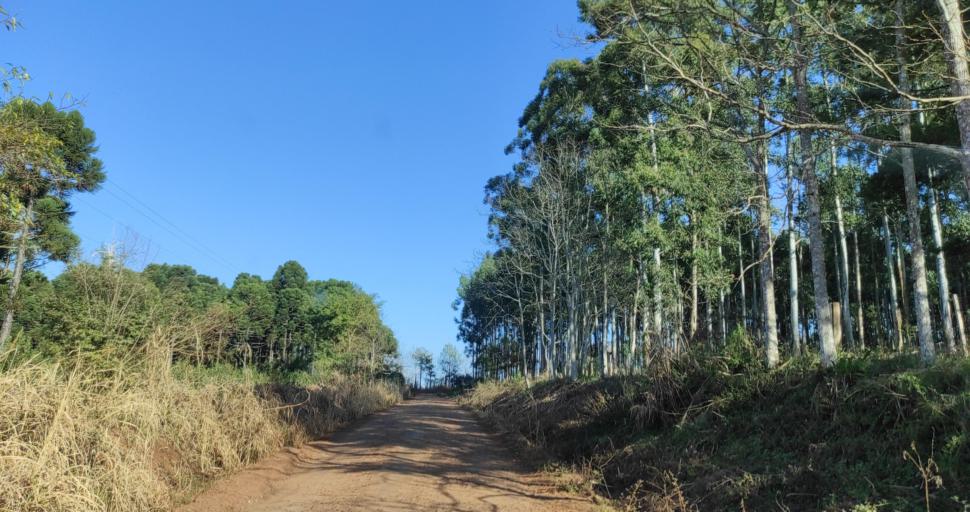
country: AR
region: Misiones
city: Puerto Rico
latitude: -26.8618
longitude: -55.0244
